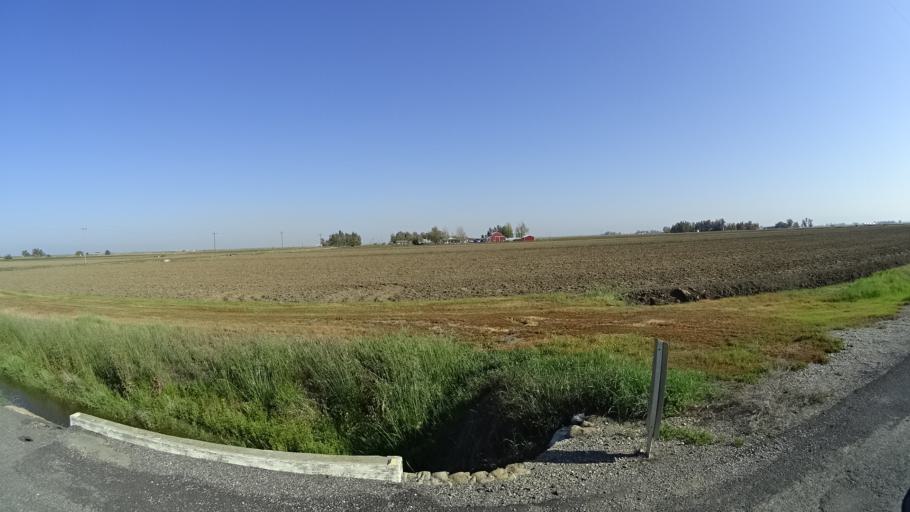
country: US
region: California
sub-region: Glenn County
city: Willows
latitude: 39.5748
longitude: -122.1066
